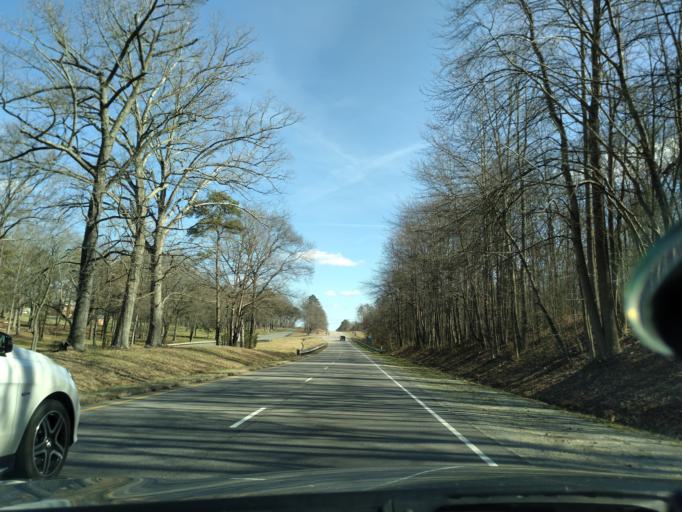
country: US
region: Virginia
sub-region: Nottoway County
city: Crewe
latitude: 37.1896
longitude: -78.1769
